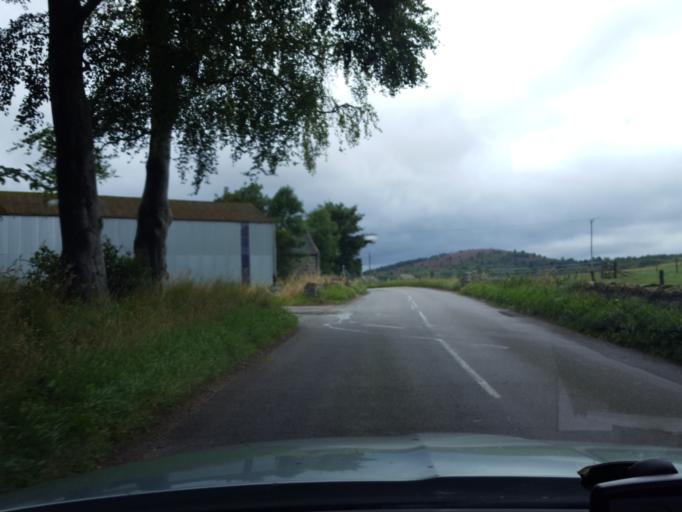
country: GB
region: Scotland
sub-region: Aberdeenshire
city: Kemnay
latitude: 57.1643
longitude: -2.4263
